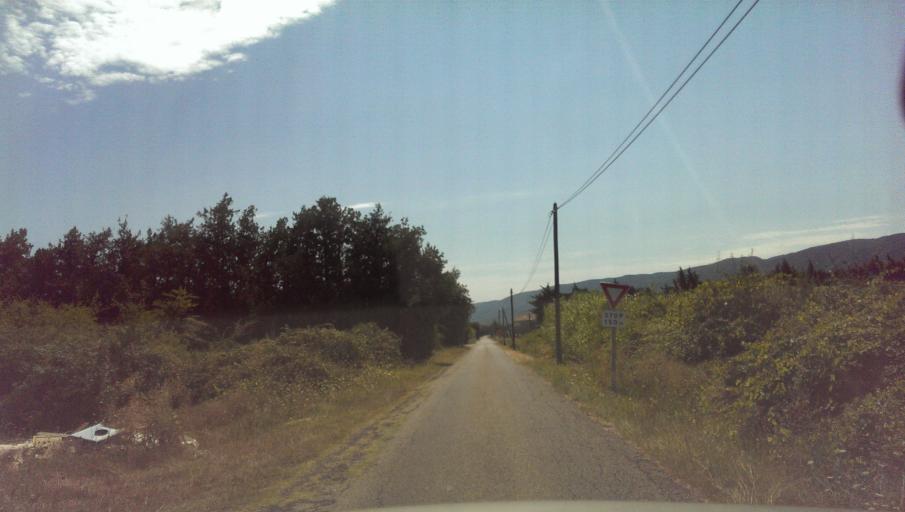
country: FR
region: Provence-Alpes-Cote d'Azur
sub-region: Departement du Vaucluse
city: Robion
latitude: 43.8682
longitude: 5.1189
